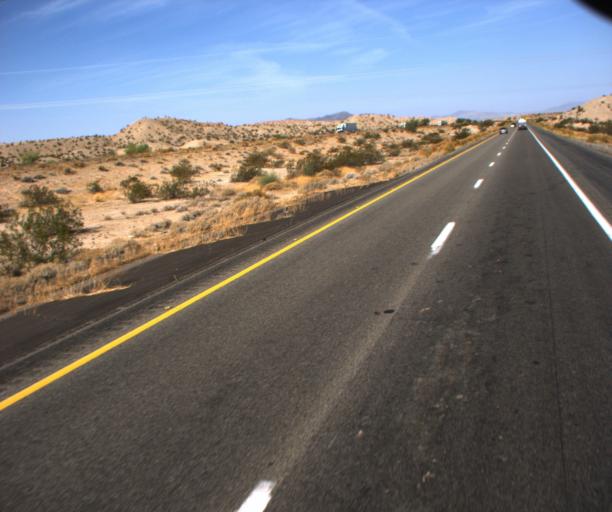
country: US
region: Arizona
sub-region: Mohave County
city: Desert Hills
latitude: 34.7275
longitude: -114.3838
